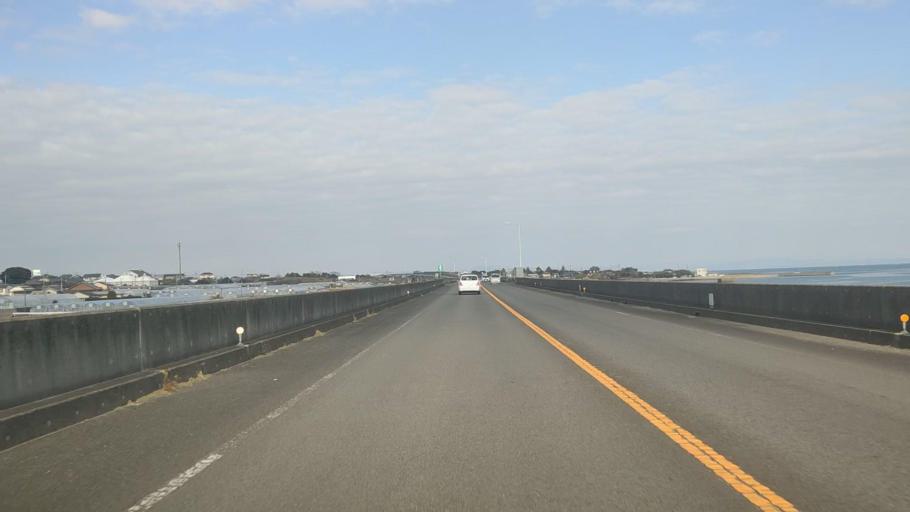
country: JP
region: Nagasaki
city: Shimabara
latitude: 32.7315
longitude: 130.3672
